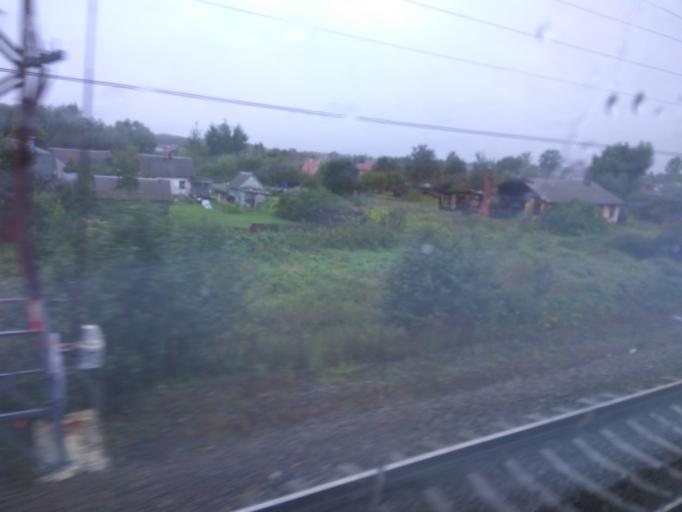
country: RU
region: Moskovskaya
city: Zhilevo
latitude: 54.9794
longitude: 38.0345
